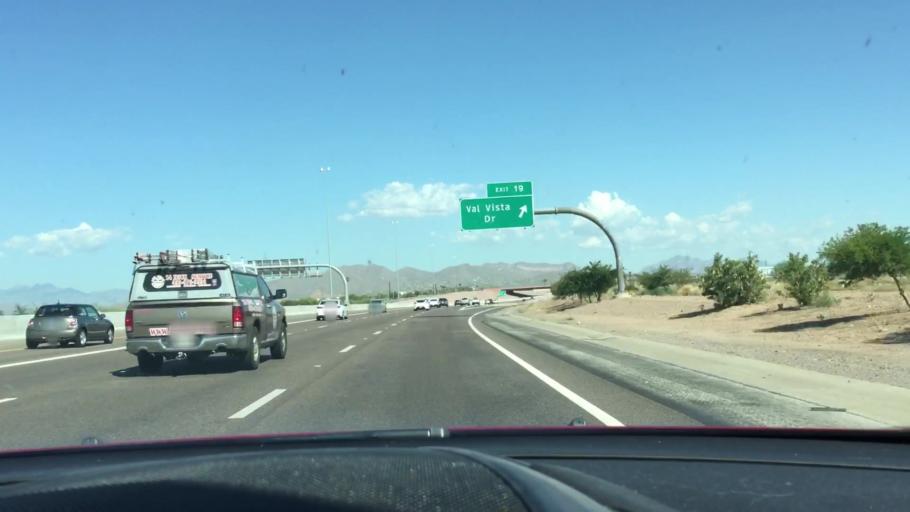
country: US
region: Arizona
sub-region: Maricopa County
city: Mesa
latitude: 33.4838
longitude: -111.7636
